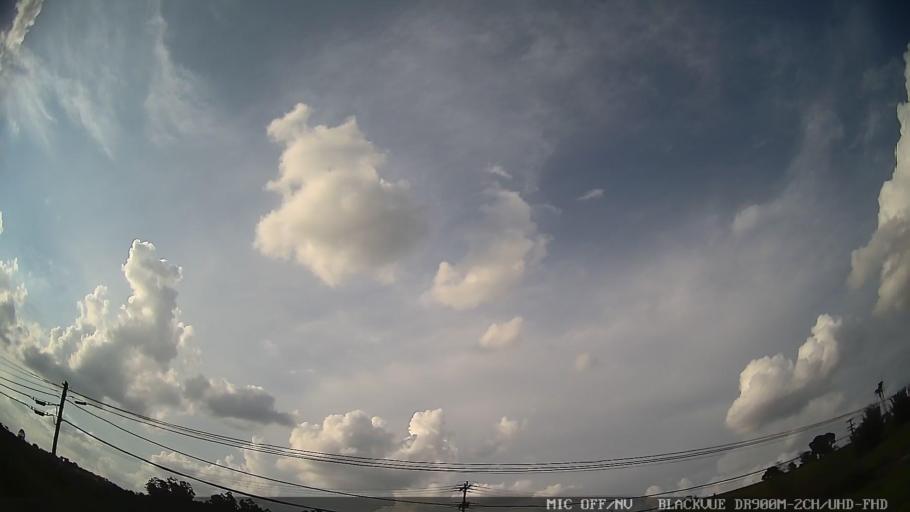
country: BR
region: Sao Paulo
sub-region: Braganca Paulista
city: Braganca Paulista
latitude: -22.9347
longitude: -46.5153
